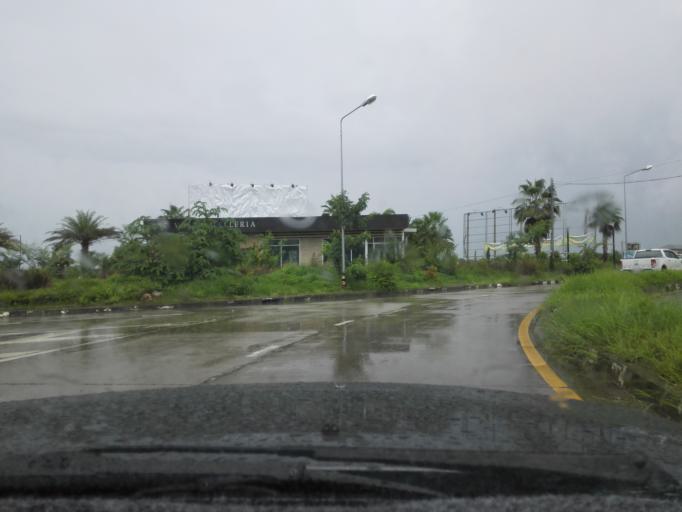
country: TH
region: Tak
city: Mae Sot
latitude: 16.7120
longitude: 98.5841
